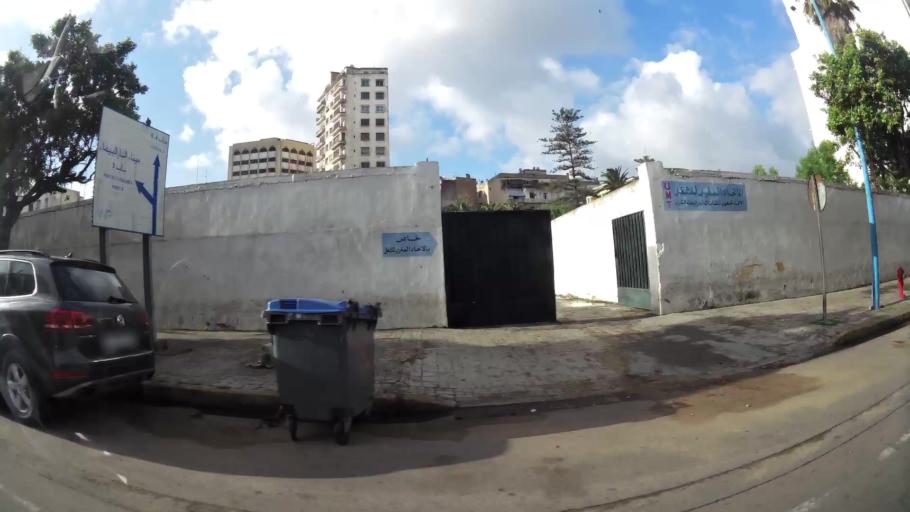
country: MA
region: Grand Casablanca
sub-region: Casablanca
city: Casablanca
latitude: 33.5962
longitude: -7.6044
